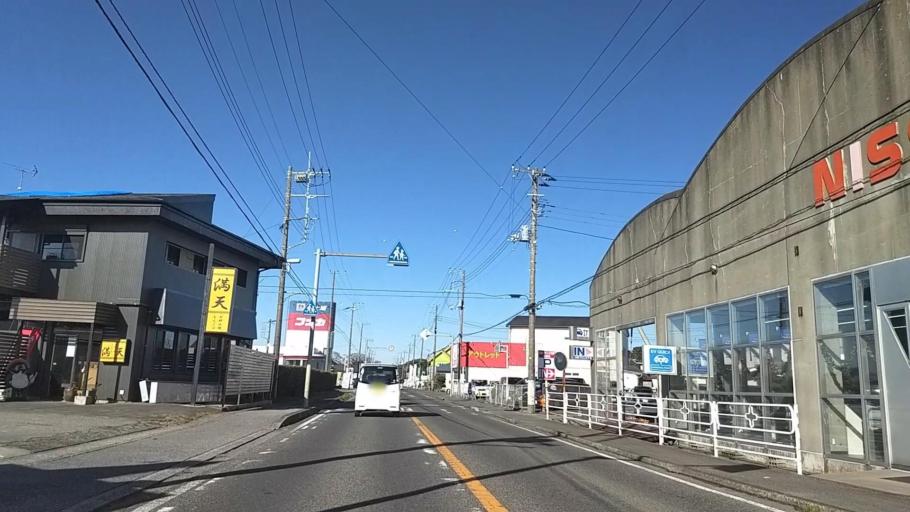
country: JP
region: Chiba
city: Ohara
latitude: 35.2799
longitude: 140.3934
